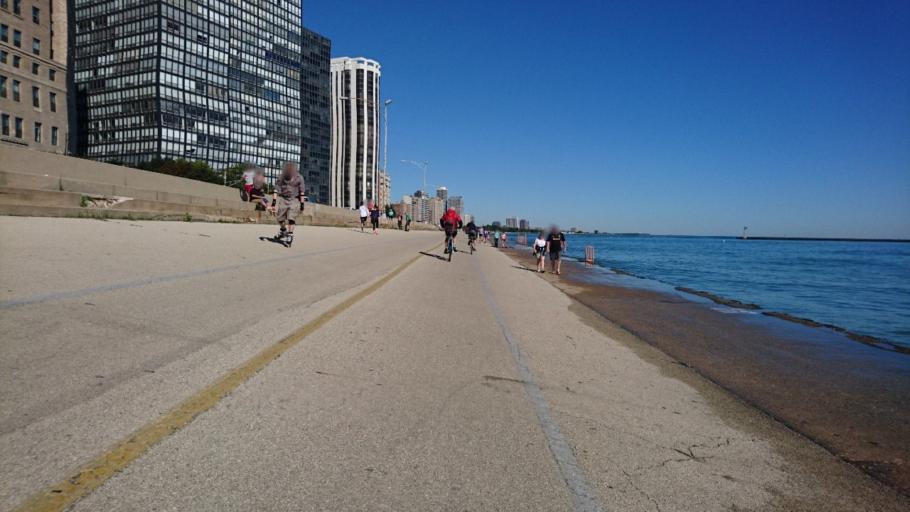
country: US
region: Illinois
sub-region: Cook County
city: Chicago
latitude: 41.8977
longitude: -87.6171
